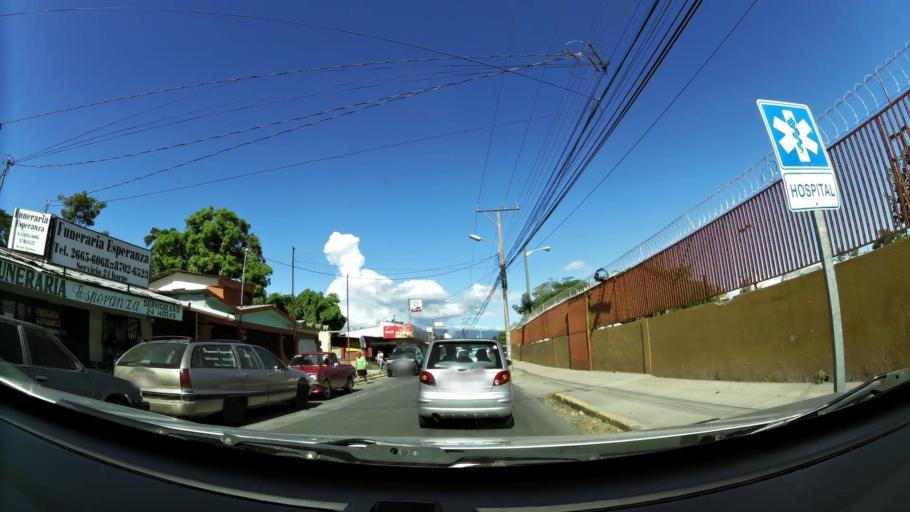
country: CR
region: Guanacaste
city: Liberia
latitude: 10.6385
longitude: -85.4325
